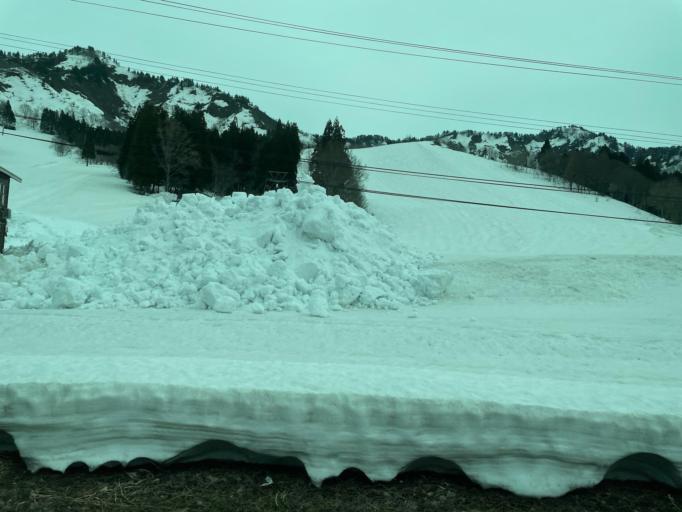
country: JP
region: Niigata
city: Shiozawa
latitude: 36.9162
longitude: 138.8496
